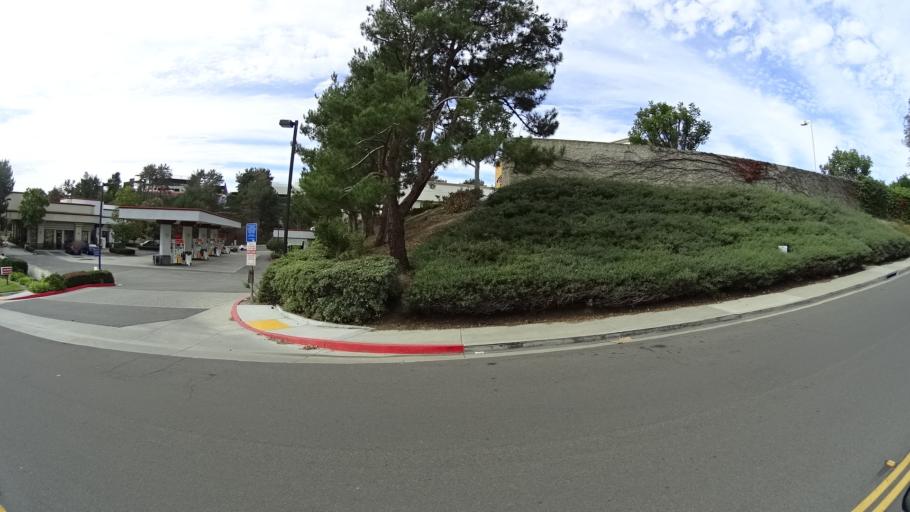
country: US
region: California
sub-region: Orange County
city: Aliso Viejo
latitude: 33.5586
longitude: -117.7232
